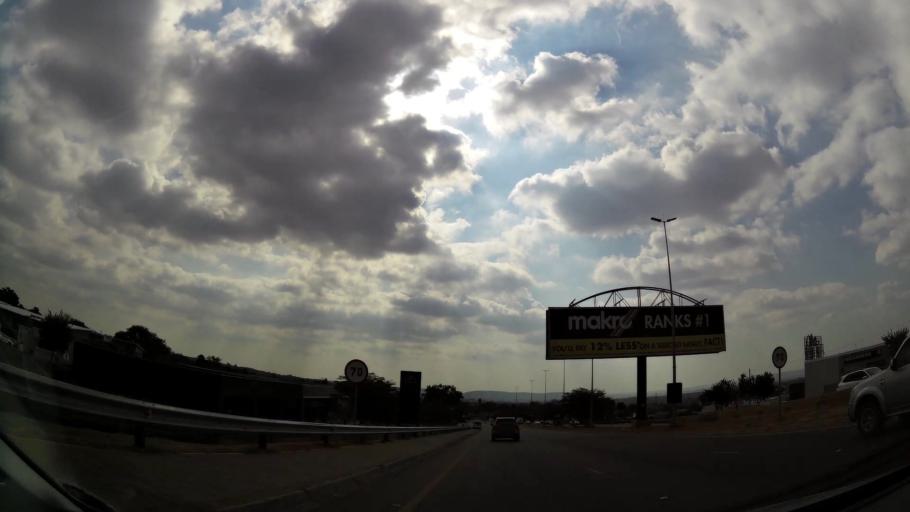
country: ZA
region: Gauteng
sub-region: City of Tshwane Metropolitan Municipality
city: Pretoria
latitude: -25.7661
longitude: 28.3214
